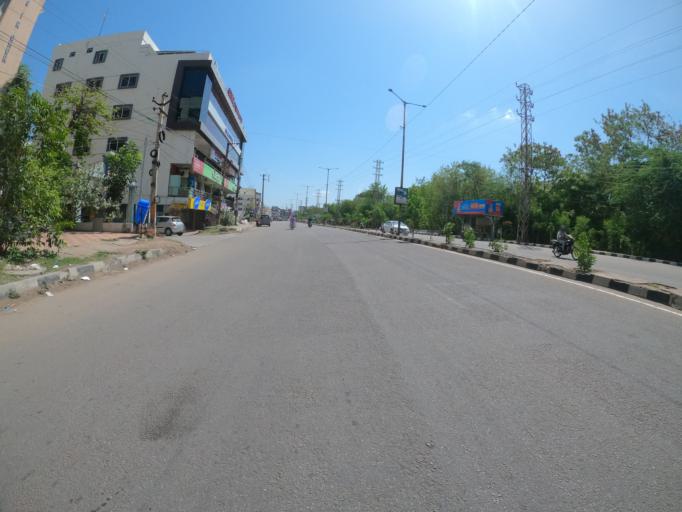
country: IN
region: Telangana
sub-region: Hyderabad
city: Hyderabad
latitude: 17.3619
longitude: 78.3935
